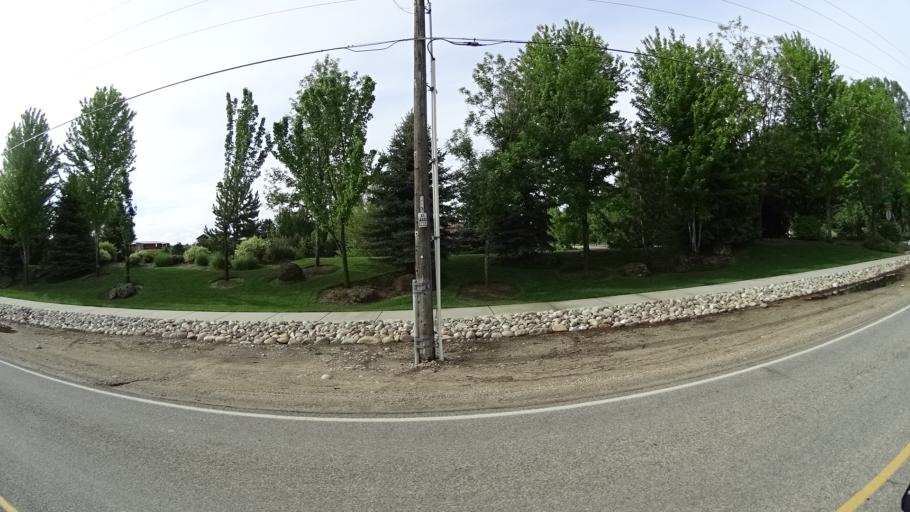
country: US
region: Idaho
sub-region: Ada County
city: Eagle
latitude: 43.7208
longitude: -116.3721
